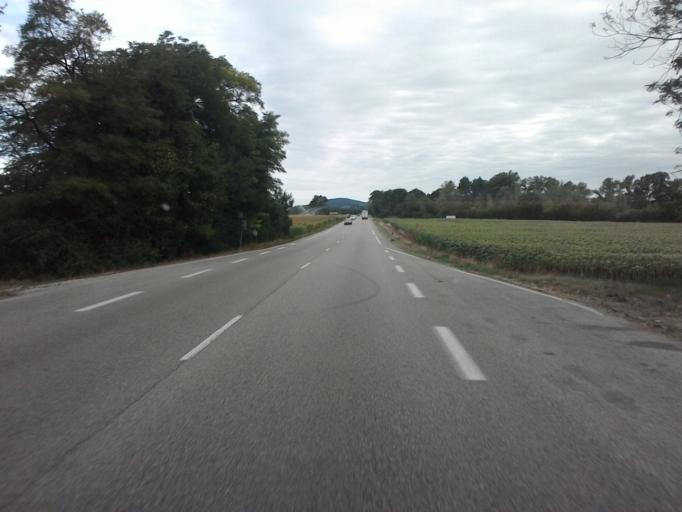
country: FR
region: Rhone-Alpes
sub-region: Departement de l'Ain
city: Ambronay
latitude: 46.0268
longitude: 5.3387
